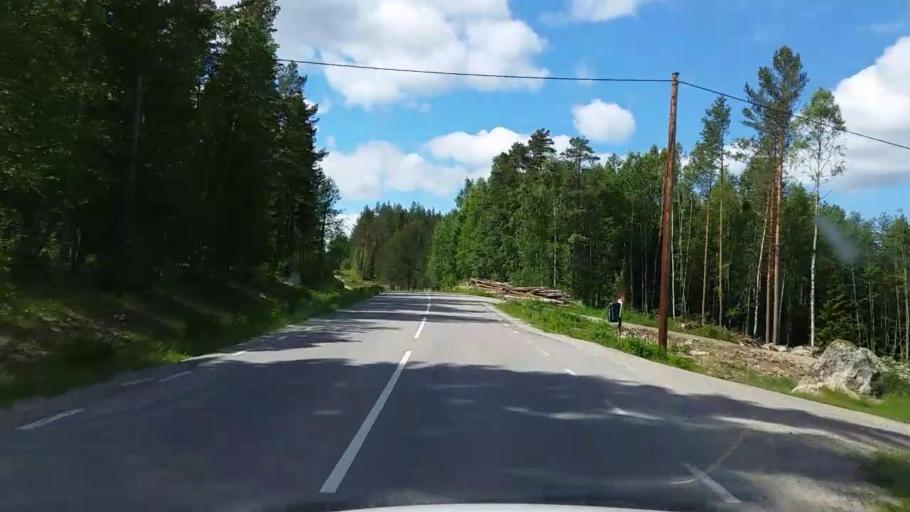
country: SE
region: Gaevleborg
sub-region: Ovanakers Kommun
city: Alfta
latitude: 61.2560
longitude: 16.1326
